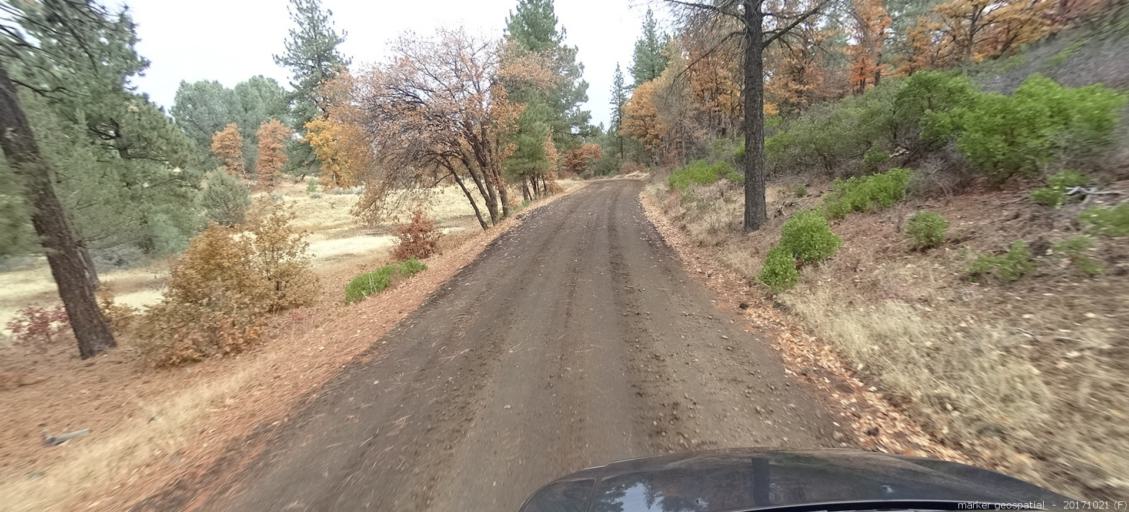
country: US
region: California
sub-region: Shasta County
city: Burney
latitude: 40.9429
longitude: -121.4410
